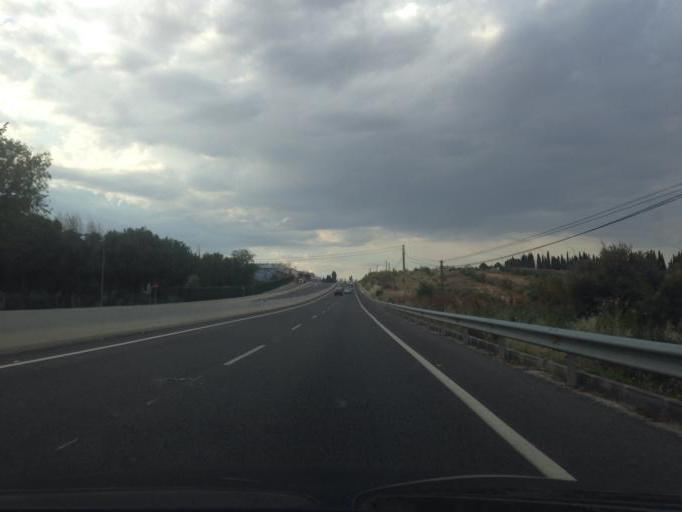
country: ES
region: Madrid
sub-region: Provincia de Madrid
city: Ajalvir
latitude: 40.4967
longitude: -3.4789
